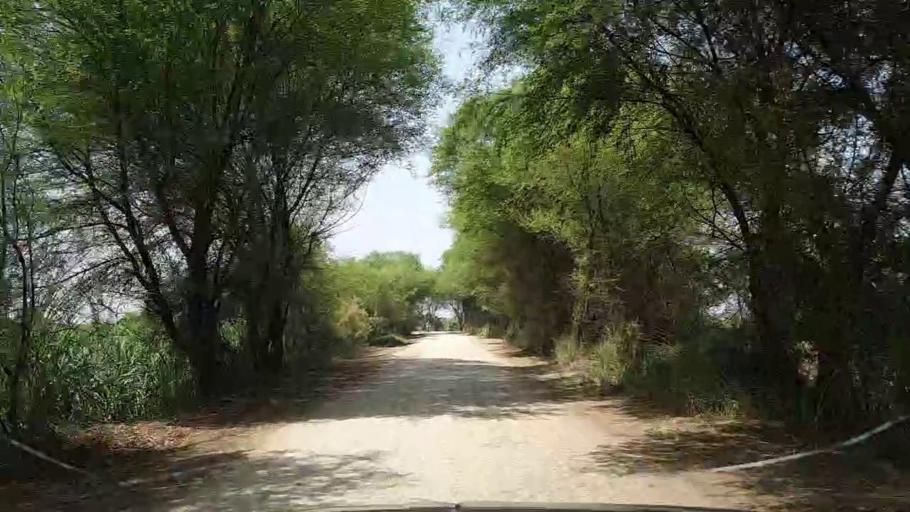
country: PK
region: Sindh
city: Ghotki
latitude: 28.0813
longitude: 69.3188
